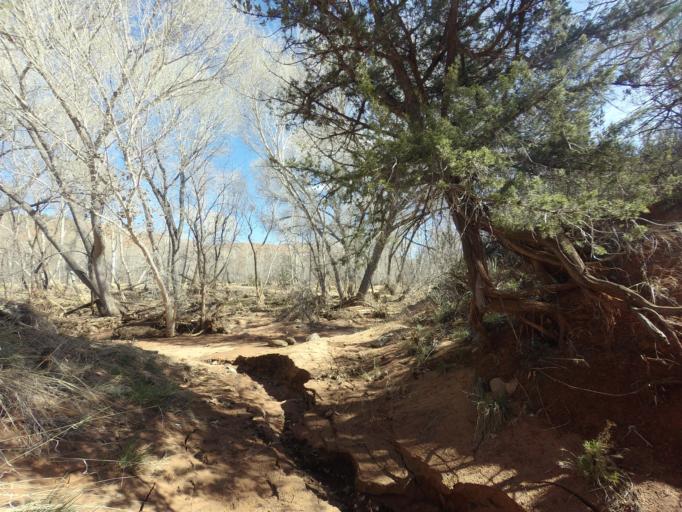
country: US
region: Arizona
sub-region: Yavapai County
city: West Sedona
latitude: 34.8243
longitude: -111.8058
